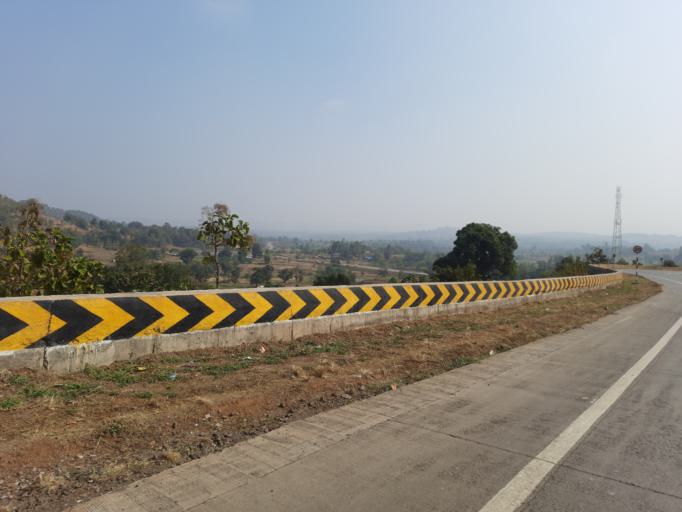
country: IN
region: Maharashtra
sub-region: Nashik Division
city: Trimbak
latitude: 20.2495
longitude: 73.5370
